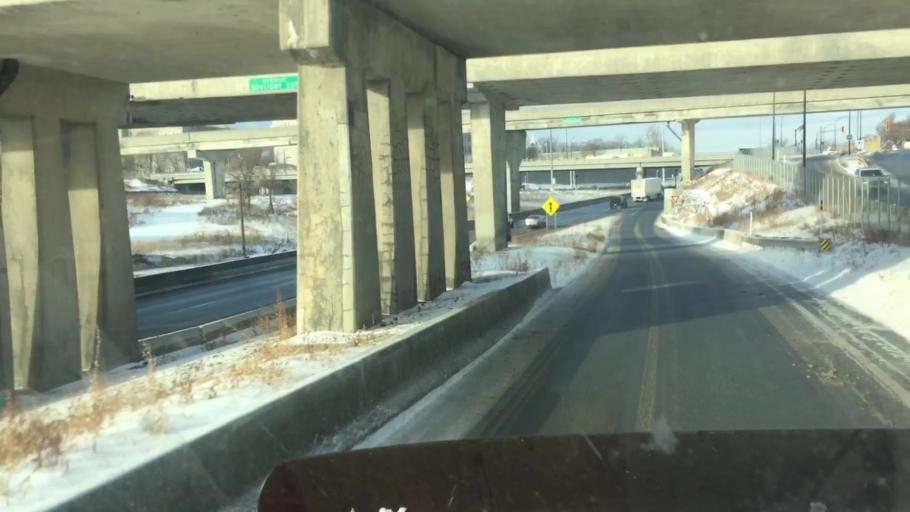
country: CA
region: Quebec
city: Montreal-Est
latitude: 45.5897
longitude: -73.5231
